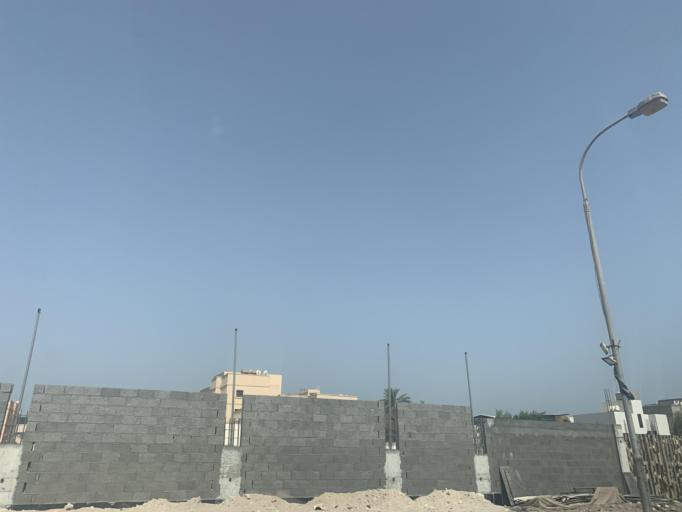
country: BH
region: Manama
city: Jidd Hafs
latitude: 26.2108
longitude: 50.4587
